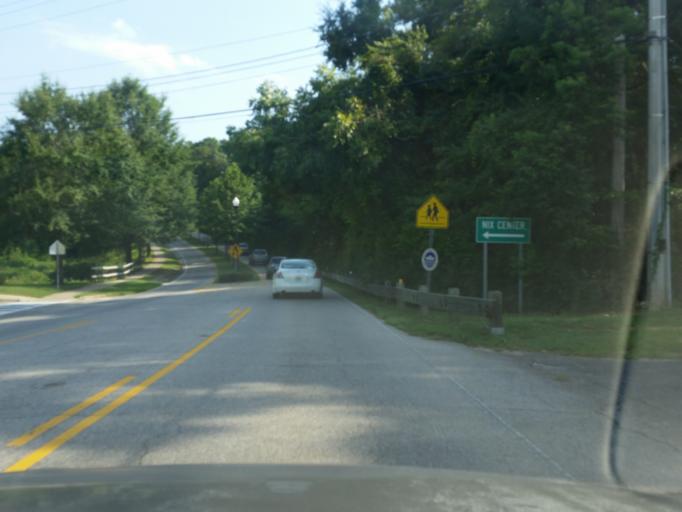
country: US
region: Alabama
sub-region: Baldwin County
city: Fairhope
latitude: 30.5302
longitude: -87.9028
